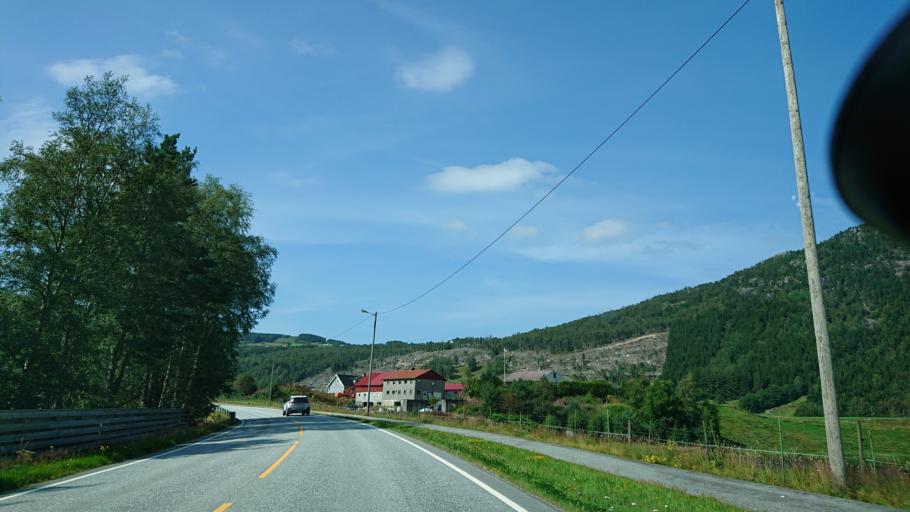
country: NO
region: Rogaland
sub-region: Strand
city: Jorpeland
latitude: 59.0740
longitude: 6.0470
